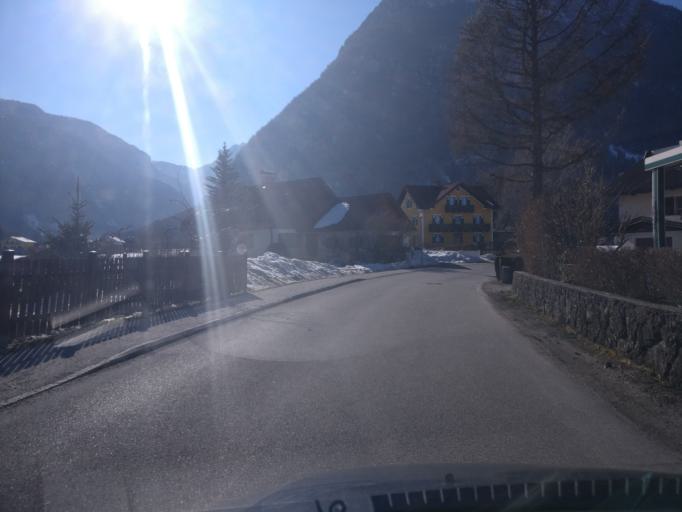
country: AT
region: Salzburg
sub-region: Politischer Bezirk Hallein
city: Golling an der Salzach
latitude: 47.5960
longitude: 13.1600
